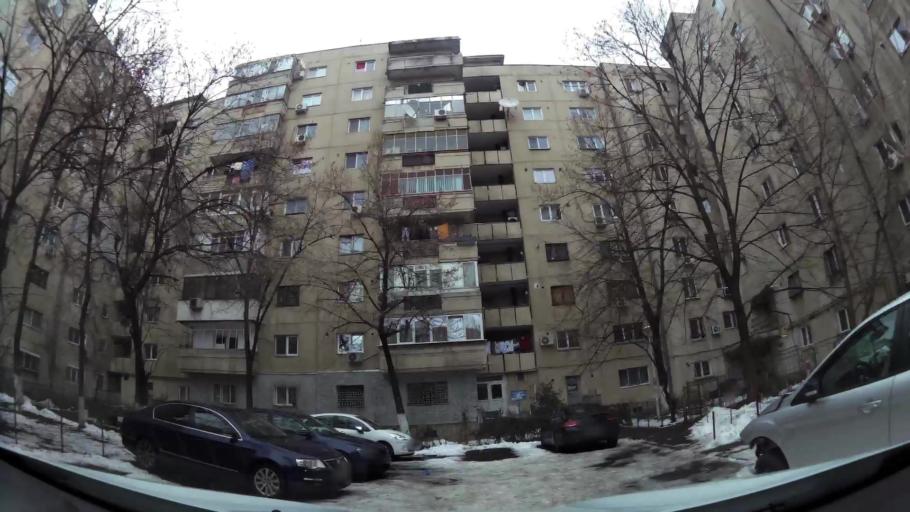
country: RO
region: Bucuresti
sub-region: Municipiul Bucuresti
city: Bucuresti
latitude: 44.4184
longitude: 26.0668
